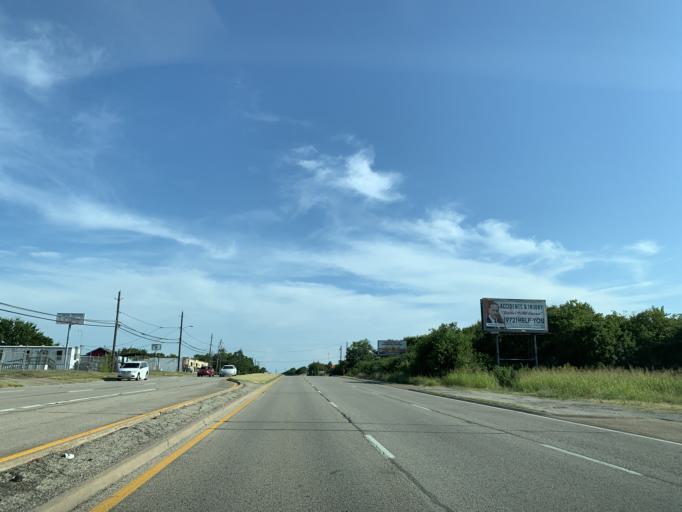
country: US
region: Texas
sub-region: Dallas County
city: Lancaster
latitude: 32.6555
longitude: -96.7830
